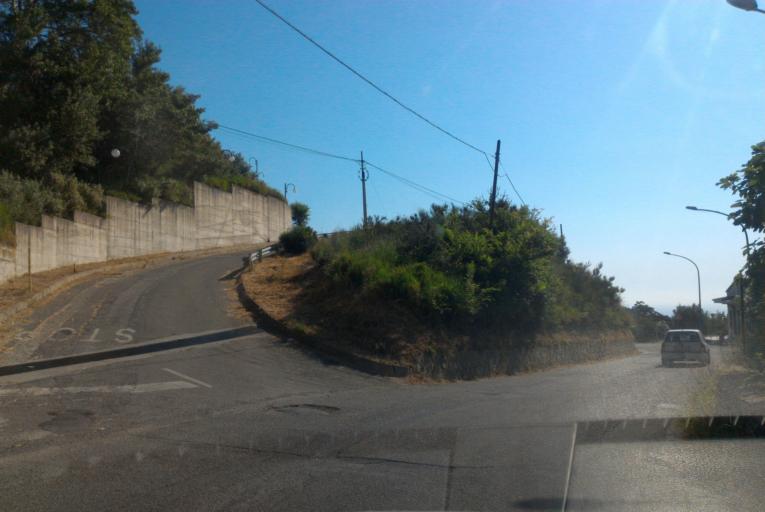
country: IT
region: Calabria
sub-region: Provincia di Crotone
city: Ciro
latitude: 39.3878
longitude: 17.0615
